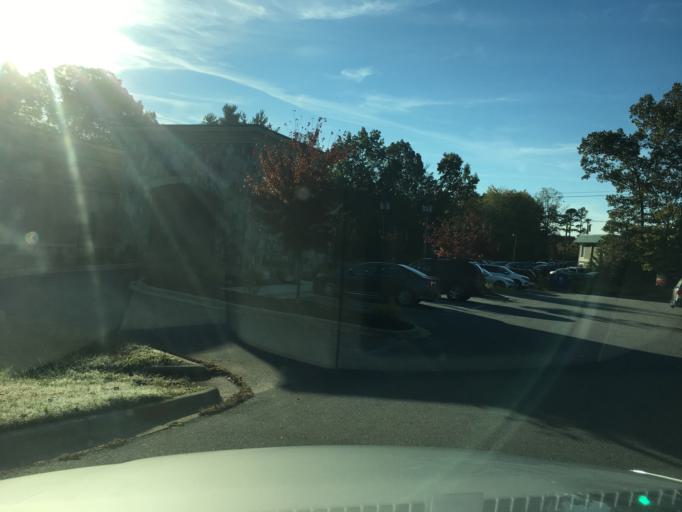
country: US
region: North Carolina
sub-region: Catawba County
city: Conover
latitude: 35.7158
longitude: -81.2652
